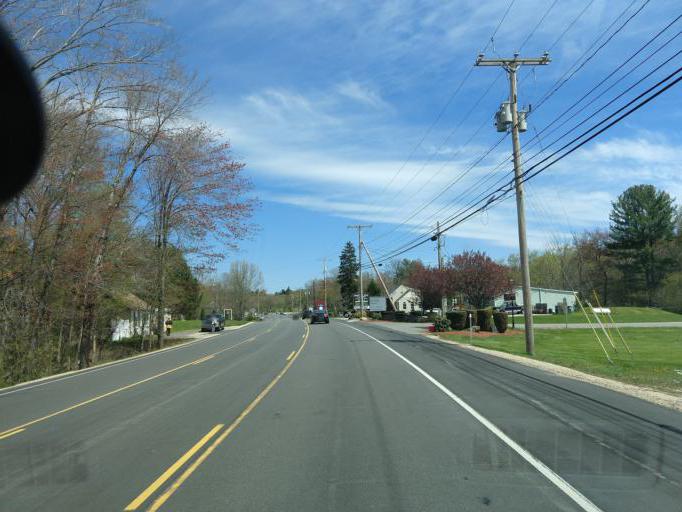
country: US
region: New Hampshire
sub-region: Rockingham County
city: Hampton Falls
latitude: 42.9056
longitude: -70.8655
